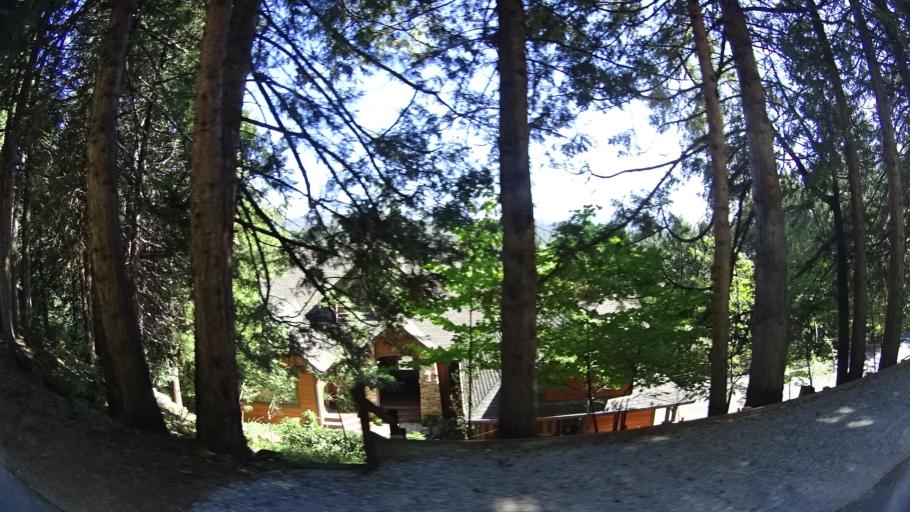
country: US
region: California
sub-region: Calaveras County
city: Arnold
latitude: 38.2521
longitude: -120.3707
